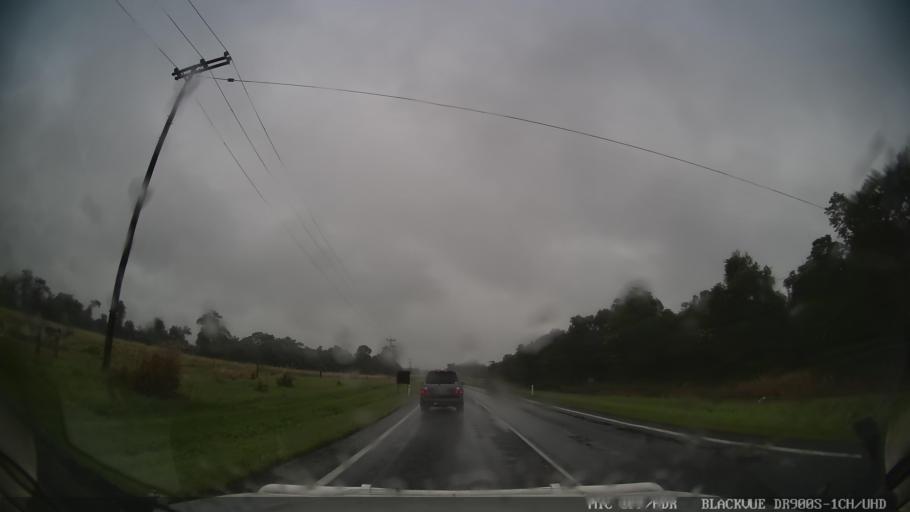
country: AU
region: Queensland
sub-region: Cassowary Coast
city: Innisfail
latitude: -17.6568
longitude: 146.0364
